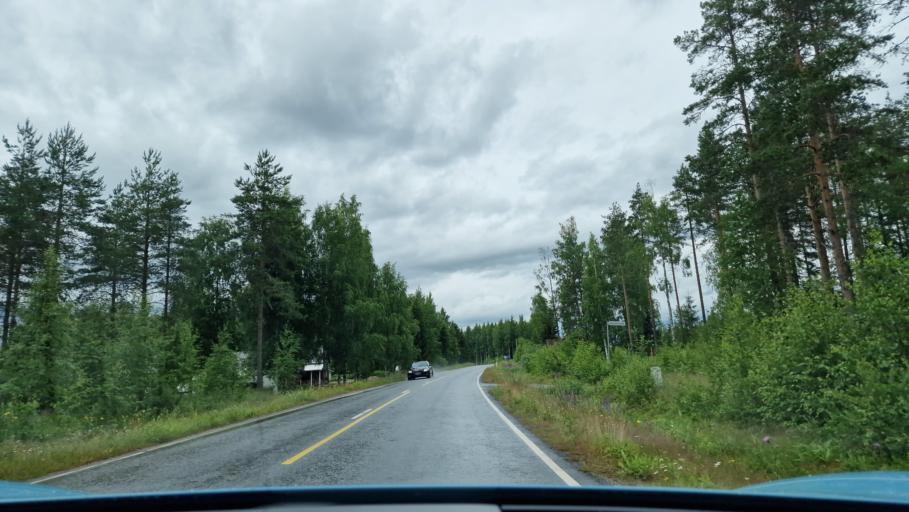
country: FI
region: Central Finland
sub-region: Saarijaervi-Viitasaari
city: Pylkoenmaeki
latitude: 62.6774
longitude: 24.5040
